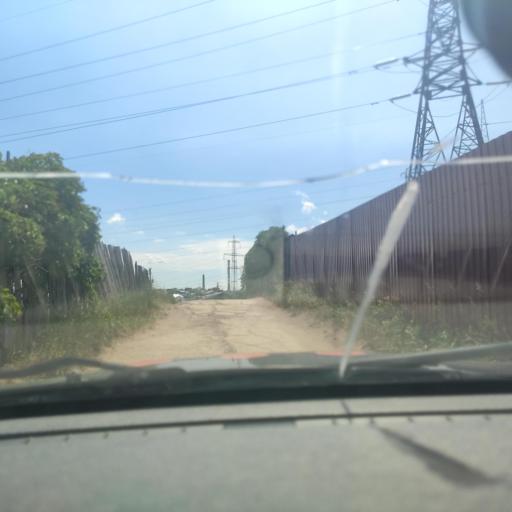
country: RU
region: Samara
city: Zhigulevsk
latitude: 53.5002
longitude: 49.4947
